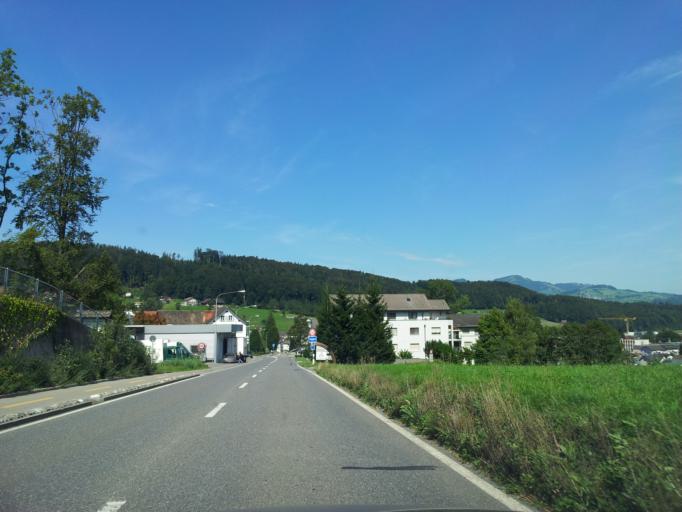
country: CH
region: Schwyz
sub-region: Bezirk March
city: Tuggen
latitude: 47.1972
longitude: 8.9383
